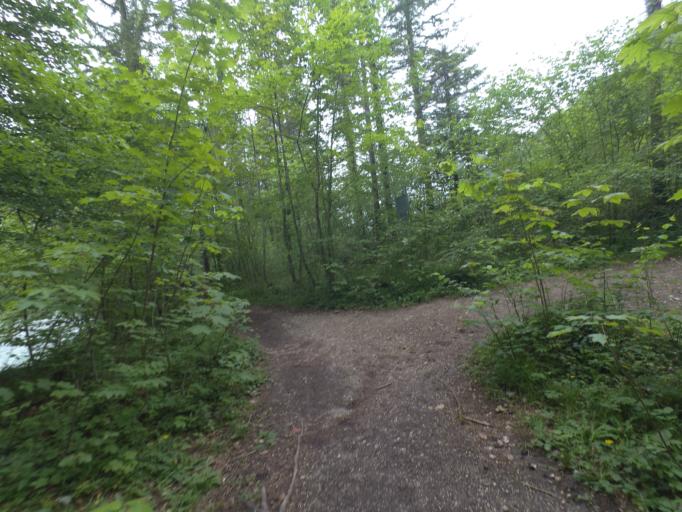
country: AT
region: Salzburg
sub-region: Politischer Bezirk Salzburg-Umgebung
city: Grodig
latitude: 47.7181
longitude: 13.0446
